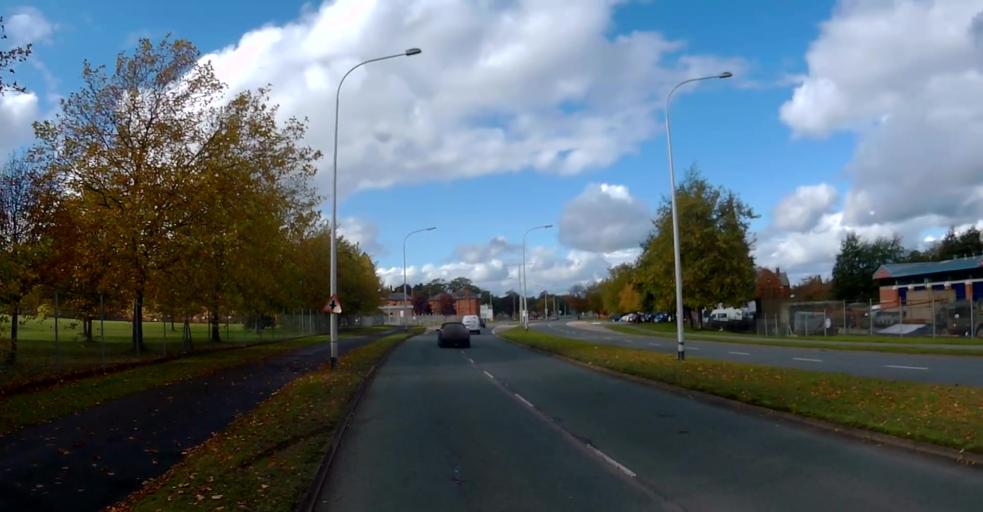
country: GB
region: England
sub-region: Hampshire
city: Aldershot
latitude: 51.2585
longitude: -0.7576
